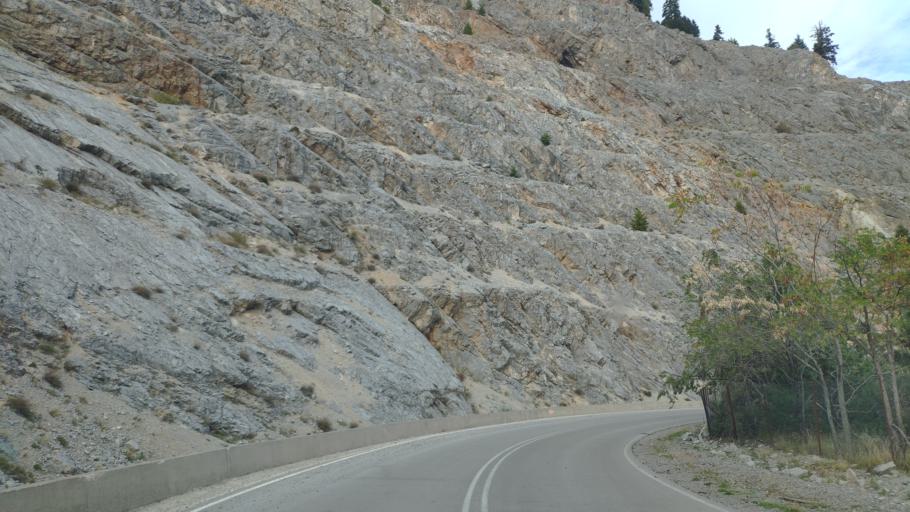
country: GR
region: Central Greece
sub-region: Nomos Fokidos
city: Amfissa
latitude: 38.6536
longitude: 22.3815
